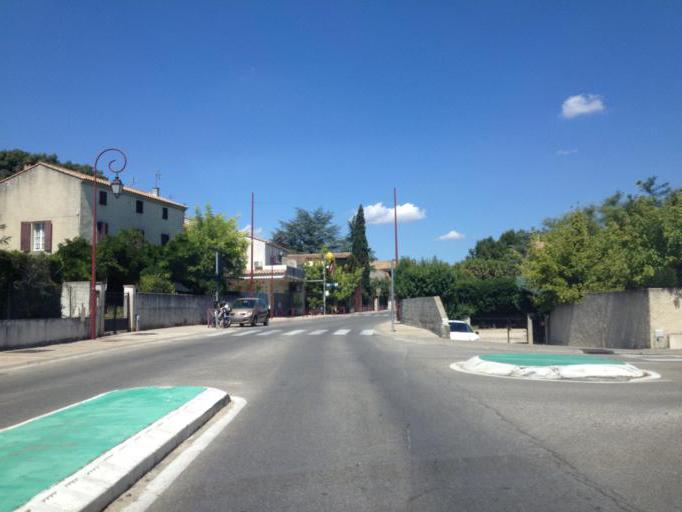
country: FR
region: Languedoc-Roussillon
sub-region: Departement du Gard
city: Sauveterre
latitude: 44.0218
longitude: 4.7935
